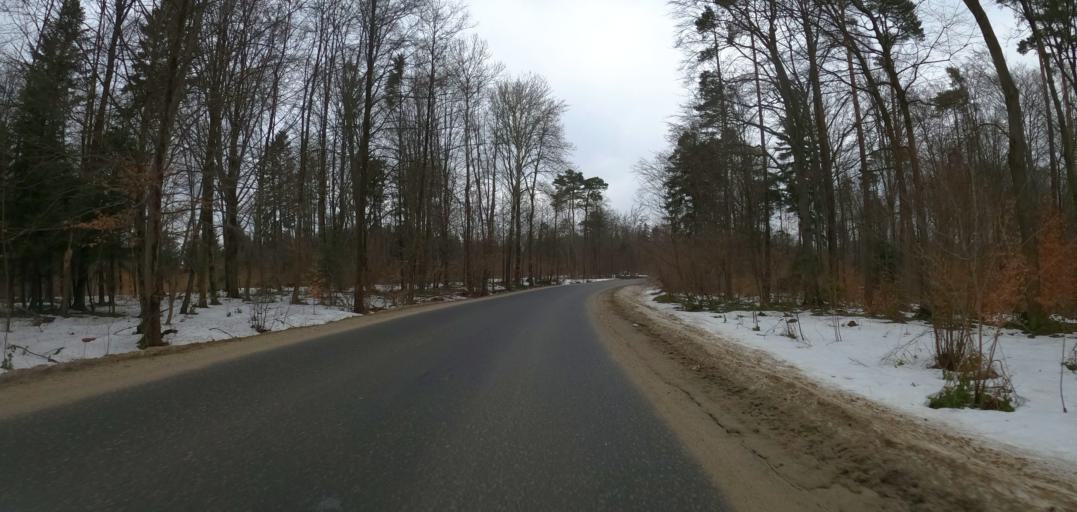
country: PL
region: Subcarpathian Voivodeship
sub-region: Powiat debicki
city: Debica
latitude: 49.9789
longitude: 21.4090
